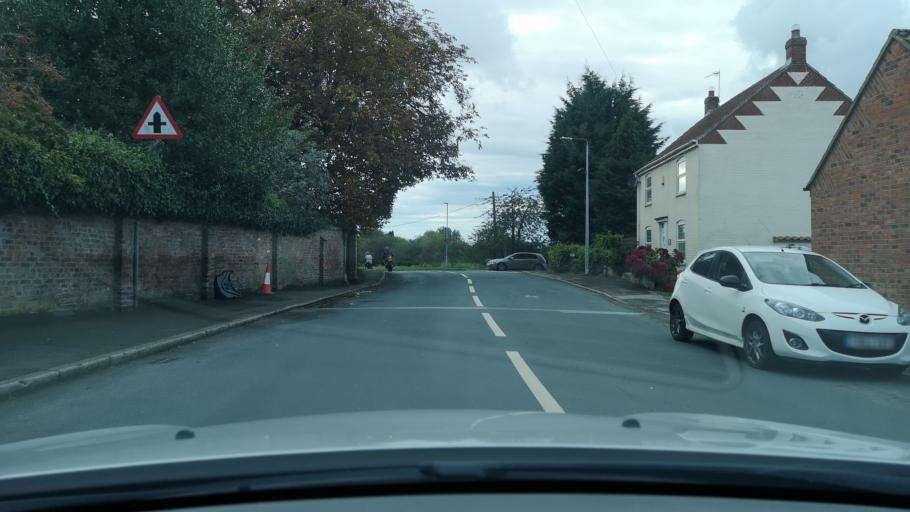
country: GB
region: England
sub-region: East Riding of Yorkshire
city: North Cave
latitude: 53.7792
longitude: -0.6523
